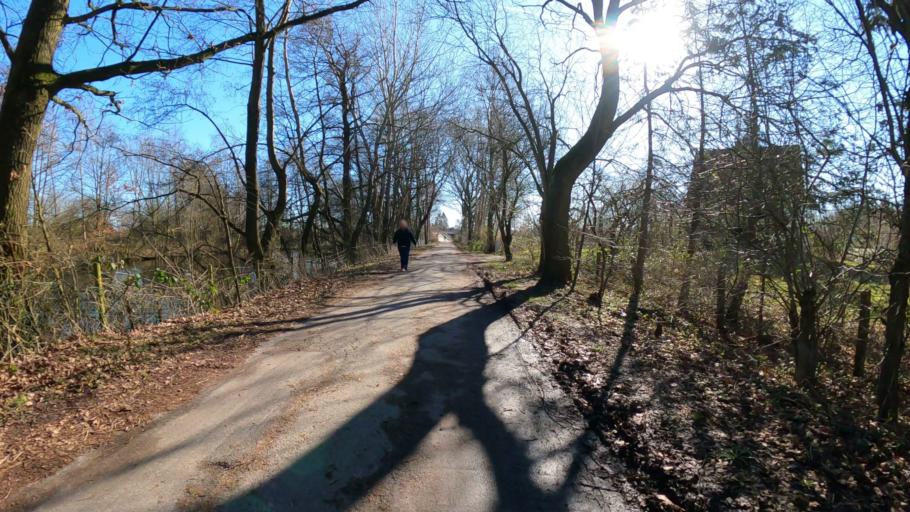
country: DE
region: Schleswig-Holstein
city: Kummerfeld
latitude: 53.6786
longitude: 9.7838
